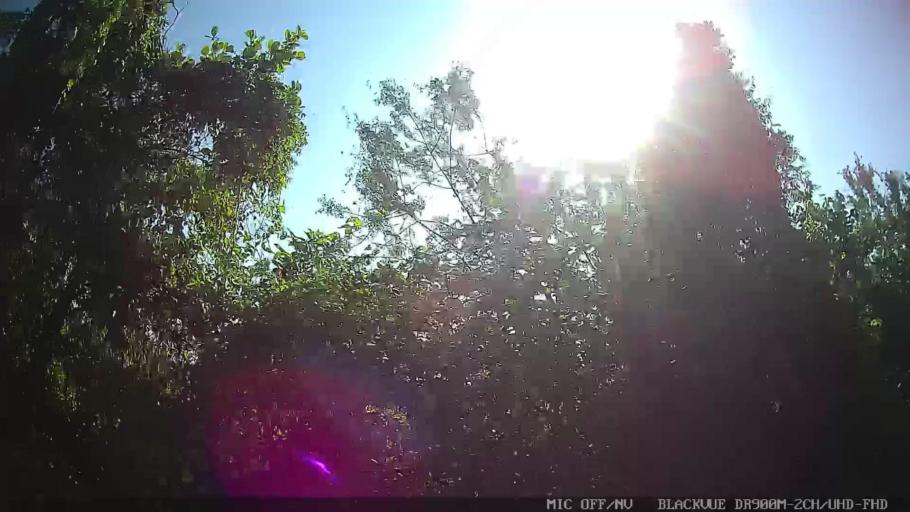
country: BR
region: Sao Paulo
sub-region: Guaruja
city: Guaruja
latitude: -24.0100
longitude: -46.2923
